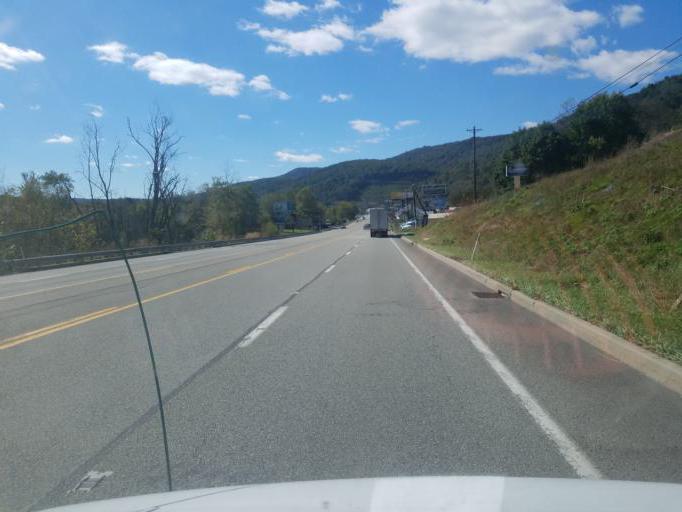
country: US
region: Pennsylvania
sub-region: Bedford County
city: Bedford
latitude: 40.0219
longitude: -78.4603
